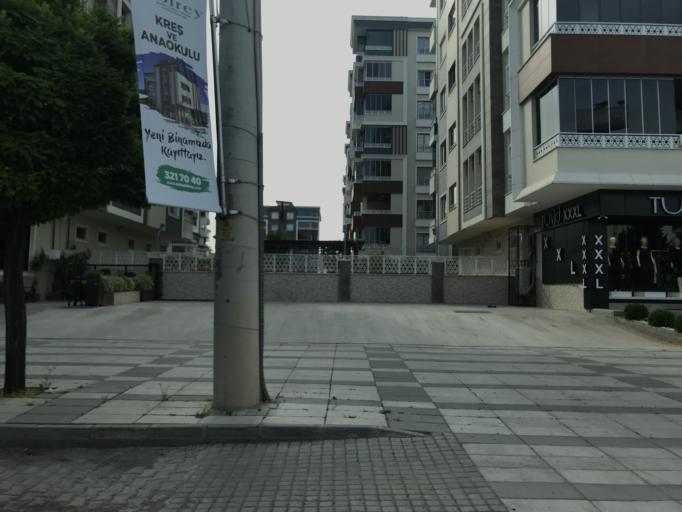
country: TR
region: Gaziantep
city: Sehitkamil
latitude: 37.0757
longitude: 37.3423
